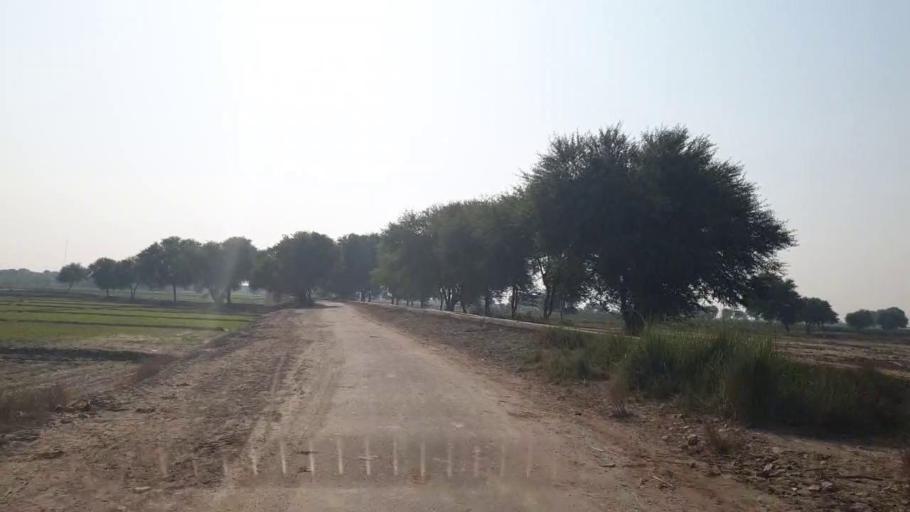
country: PK
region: Sindh
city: Sehwan
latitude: 26.4414
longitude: 67.8394
